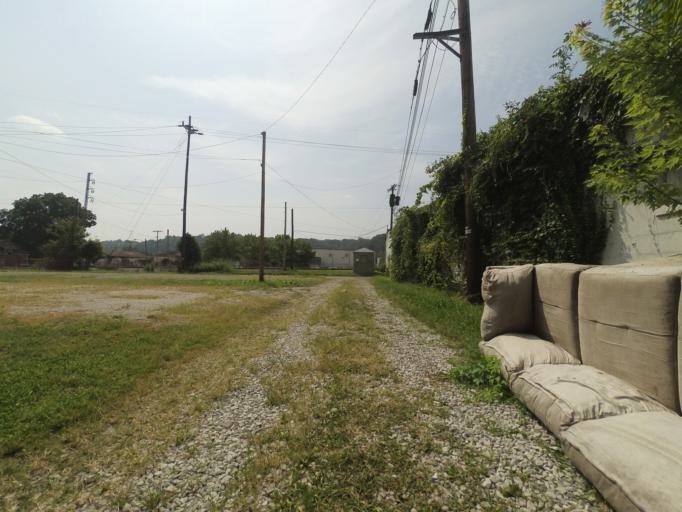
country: US
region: West Virginia
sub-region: Cabell County
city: Huntington
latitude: 38.4117
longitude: -82.4627
